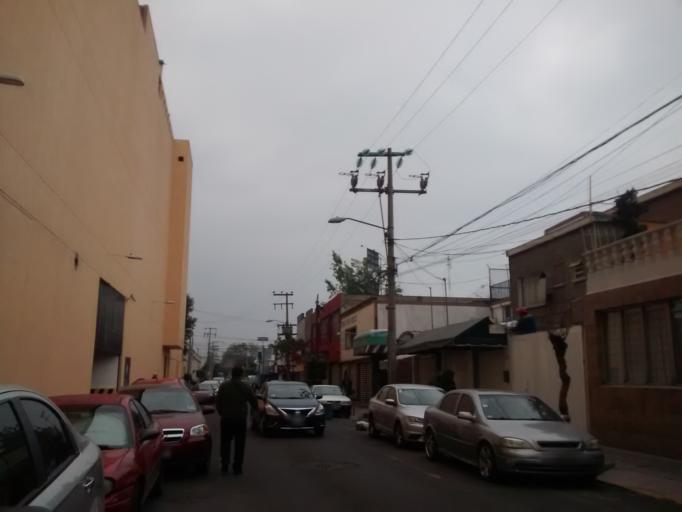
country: MX
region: Mexico
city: Colonia Lindavista
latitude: 19.4917
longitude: -99.1339
